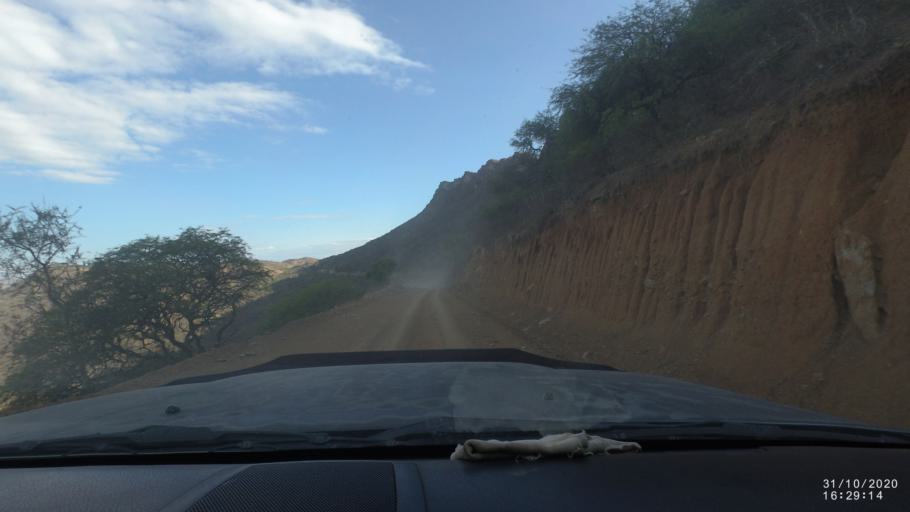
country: BO
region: Chuquisaca
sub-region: Provincia Zudanez
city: Mojocoya
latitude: -18.4184
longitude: -64.5858
